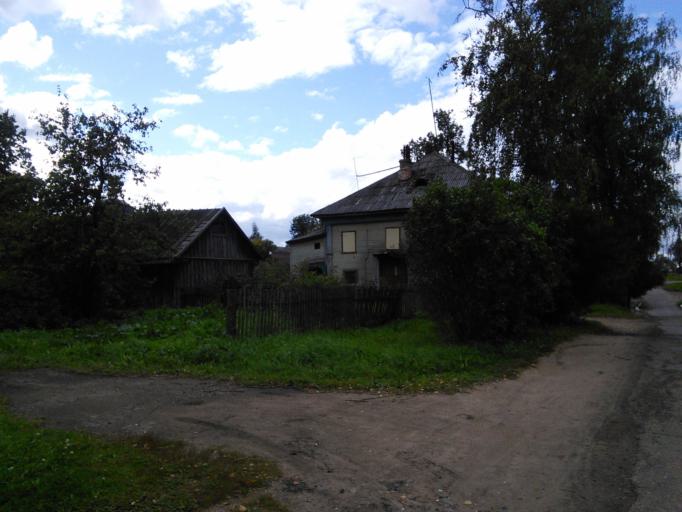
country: RU
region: Jaroslavl
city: Myshkin
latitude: 57.7862
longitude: 38.4512
